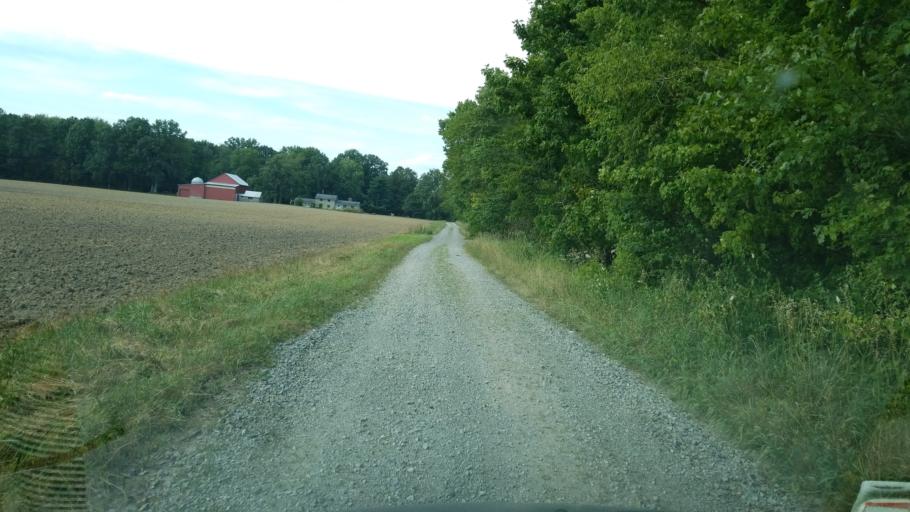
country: US
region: Ohio
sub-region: Delaware County
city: Ashley
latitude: 40.4155
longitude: -83.0591
